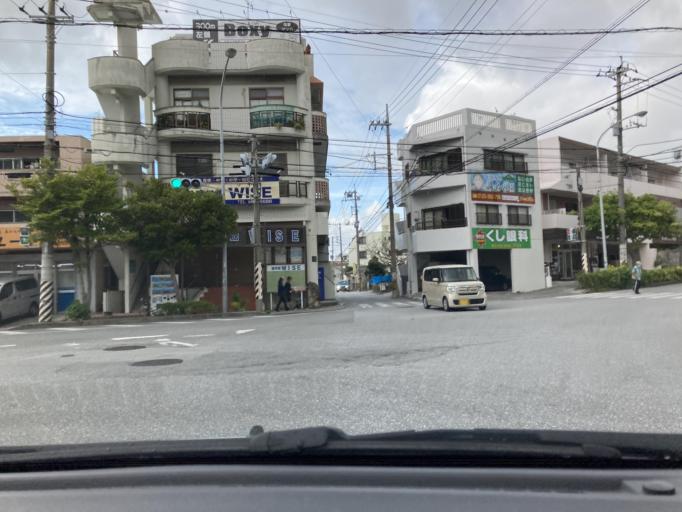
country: JP
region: Okinawa
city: Naha-shi
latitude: 26.2020
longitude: 127.6972
